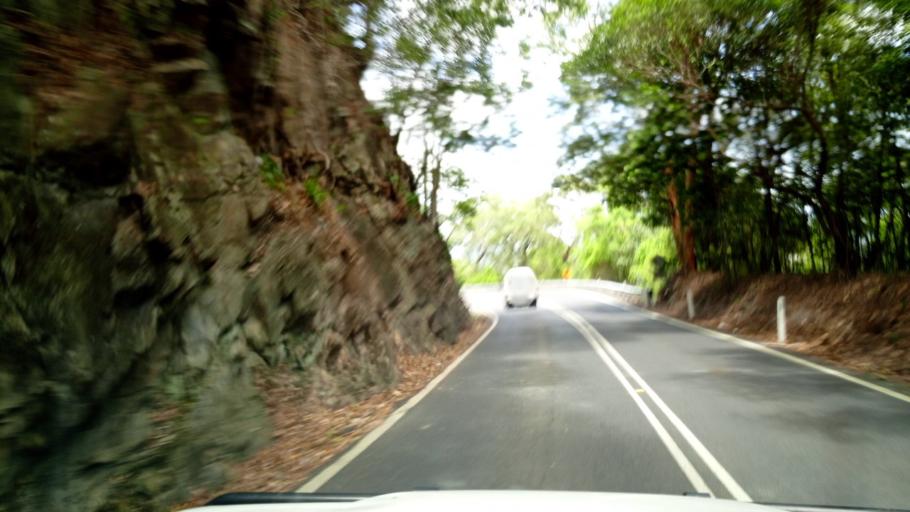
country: AU
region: Queensland
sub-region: Cairns
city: Redlynch
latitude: -16.8462
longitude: 145.6829
